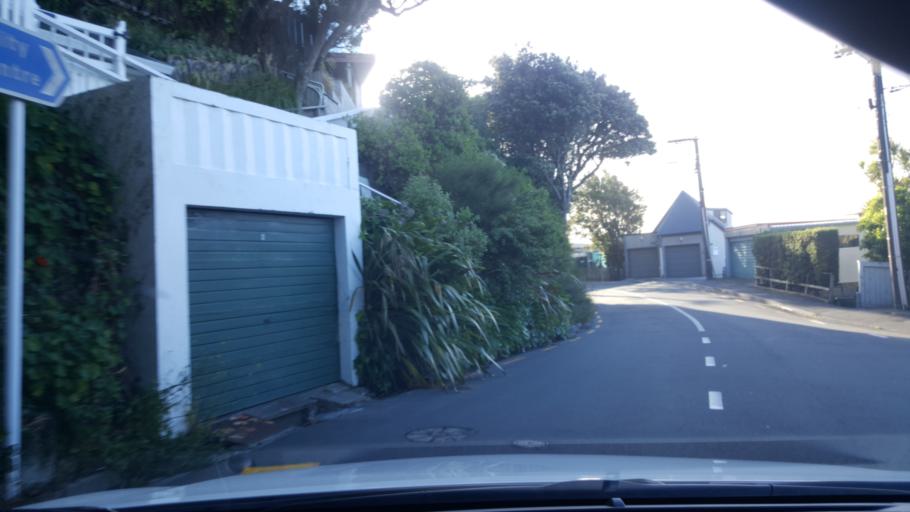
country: NZ
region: Wellington
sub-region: Wellington City
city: Wellington
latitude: -41.2933
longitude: 174.7983
